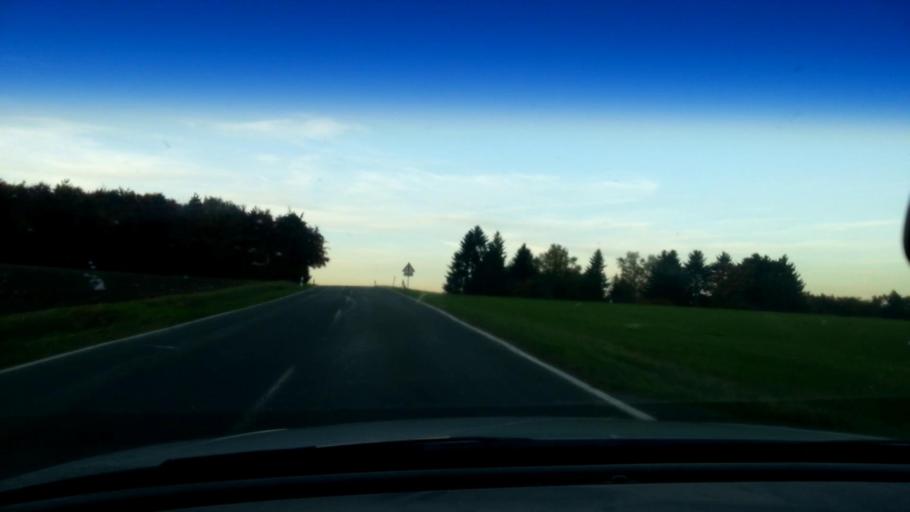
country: DE
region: Bavaria
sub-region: Upper Franconia
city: Heiligenstadt
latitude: 49.8488
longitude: 11.1169
